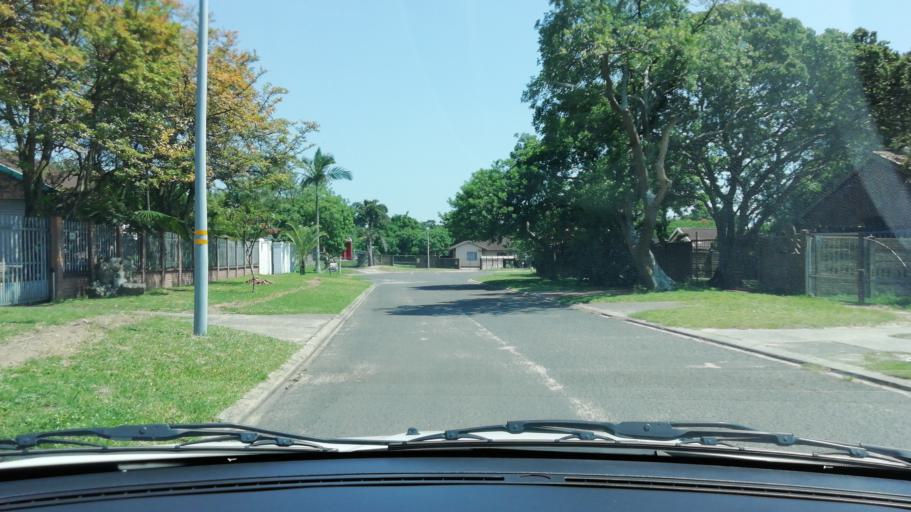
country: ZA
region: KwaZulu-Natal
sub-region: uThungulu District Municipality
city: Richards Bay
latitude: -28.7388
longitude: 32.0599
